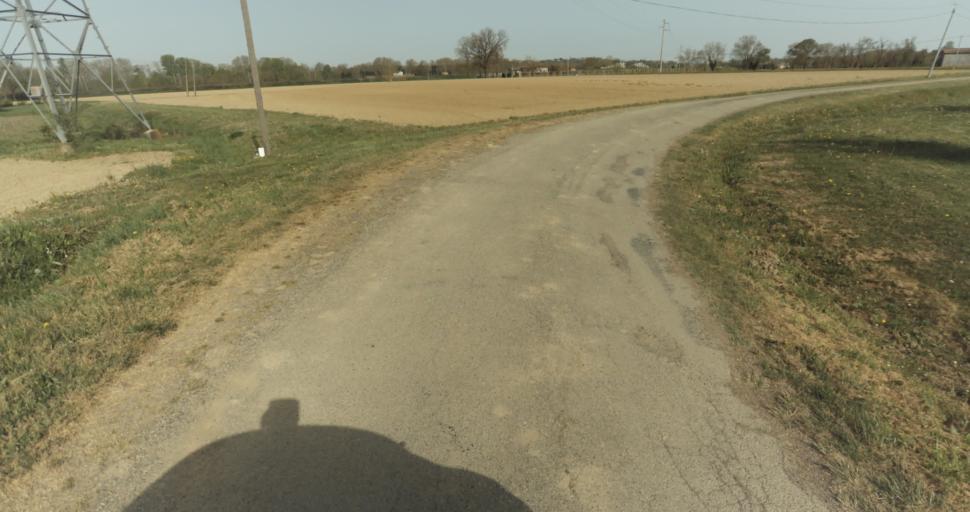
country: FR
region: Midi-Pyrenees
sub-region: Departement du Tarn-et-Garonne
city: Moissac
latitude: 44.0806
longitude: 1.1080
